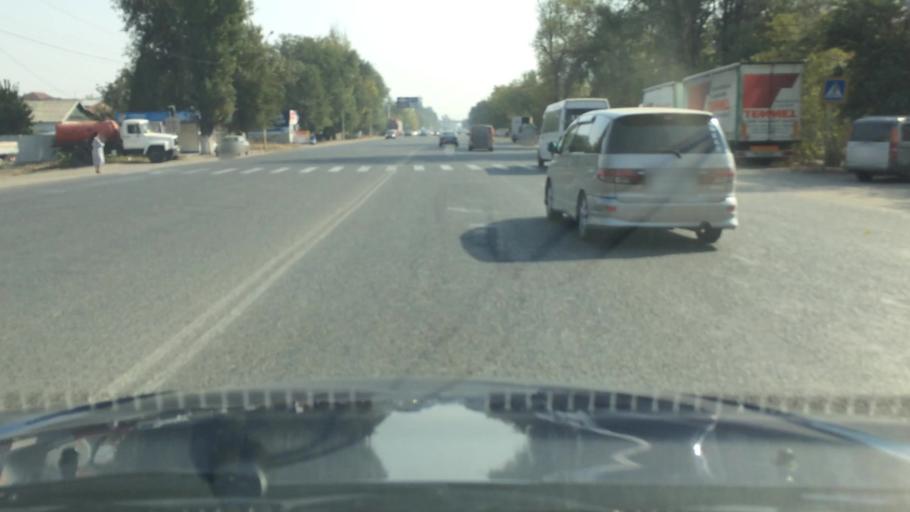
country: KG
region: Chuy
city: Lebedinovka
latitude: 42.8868
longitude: 74.6721
